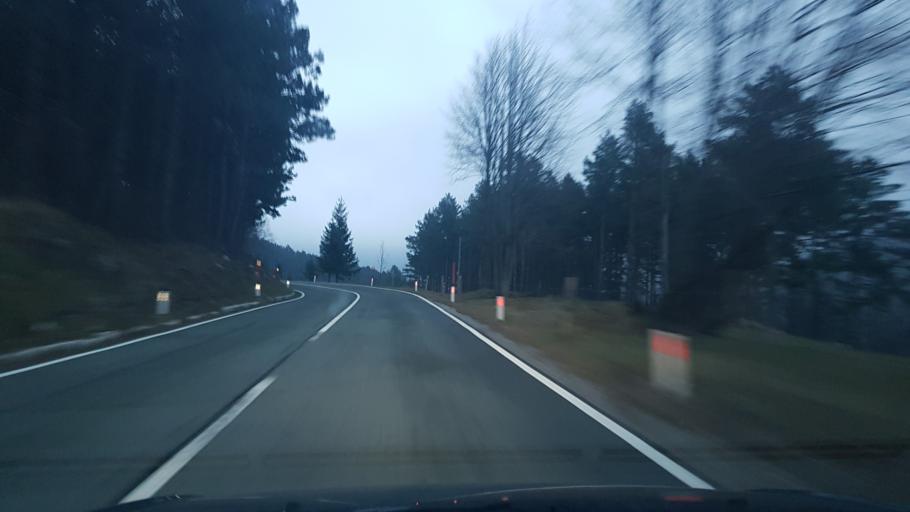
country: SI
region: Vipava
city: Vipava
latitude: 45.8895
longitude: 14.0098
